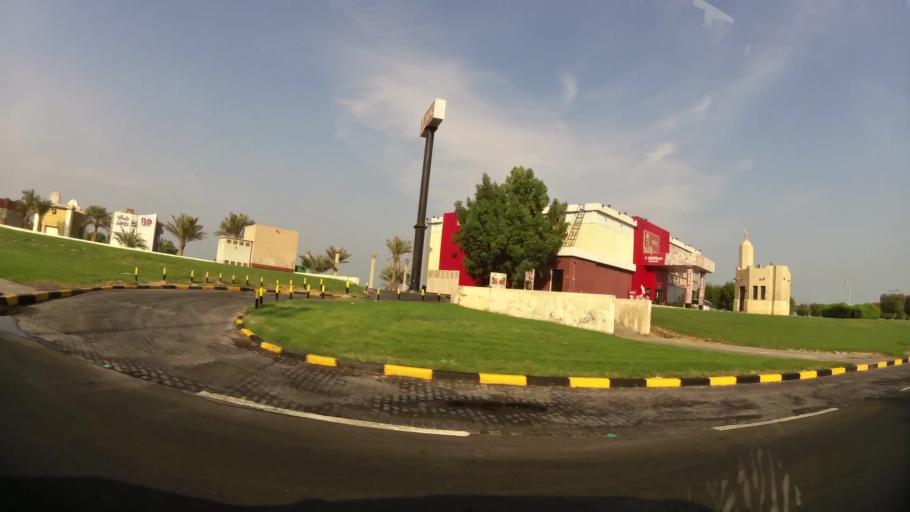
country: KW
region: Al Asimah
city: Ad Dasmah
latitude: 29.3731
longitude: 48.0071
